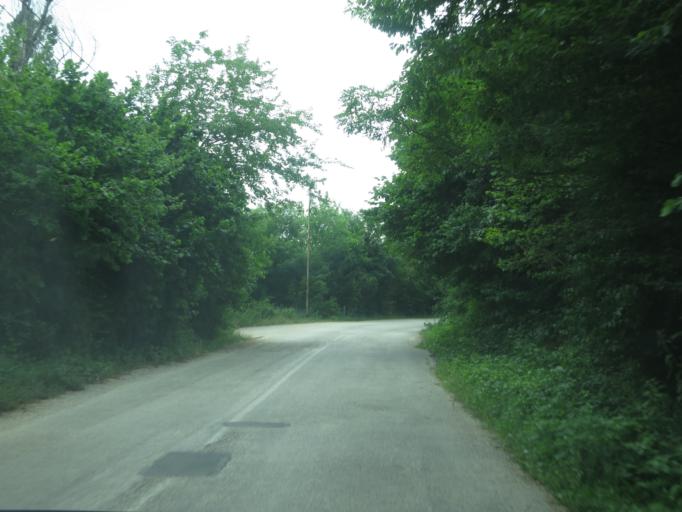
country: GE
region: Kakheti
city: Sighnaghi
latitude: 41.6100
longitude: 45.9271
